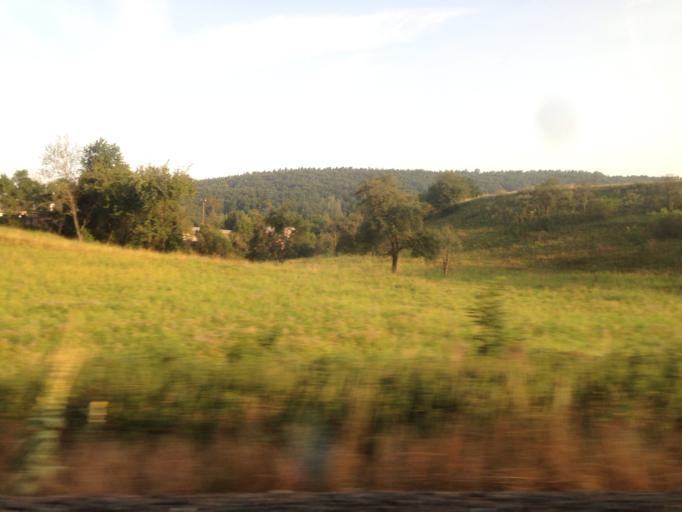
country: DE
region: Thuringia
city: Grosspurschutz
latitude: 50.8230
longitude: 11.5893
